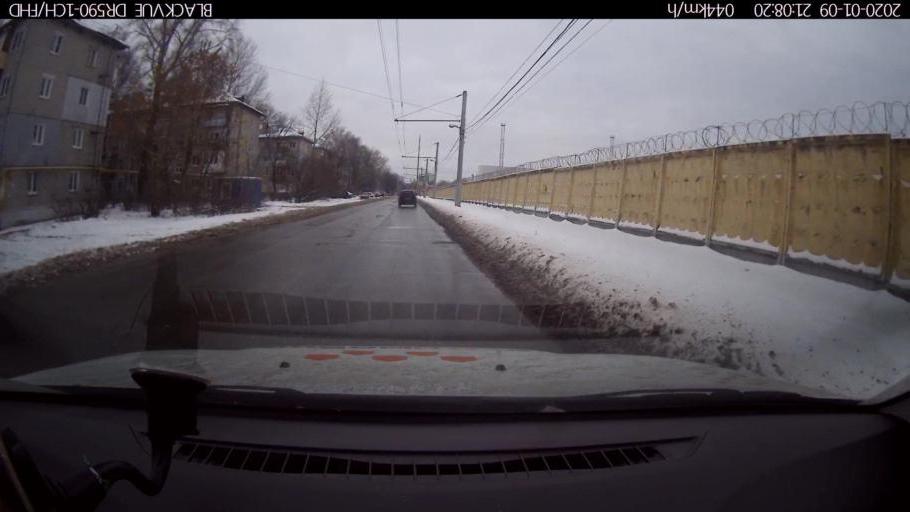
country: RU
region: Nizjnij Novgorod
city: Gorbatovka
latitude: 56.2943
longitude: 43.8659
